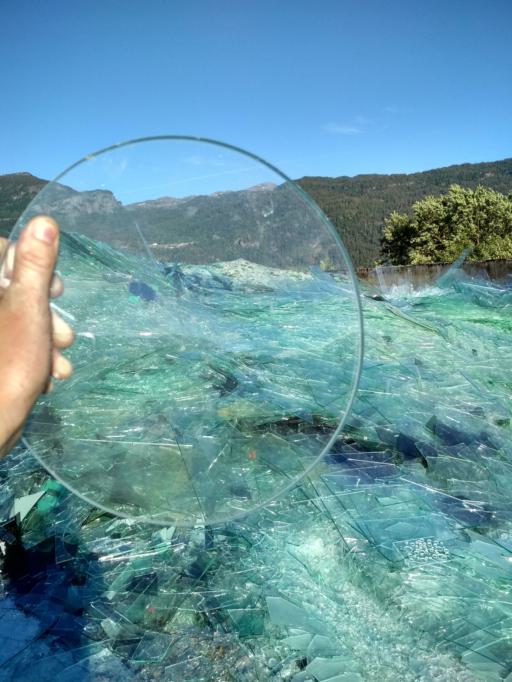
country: NO
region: Rogaland
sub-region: Sauda
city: Sauda
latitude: 59.6413
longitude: 6.3181
